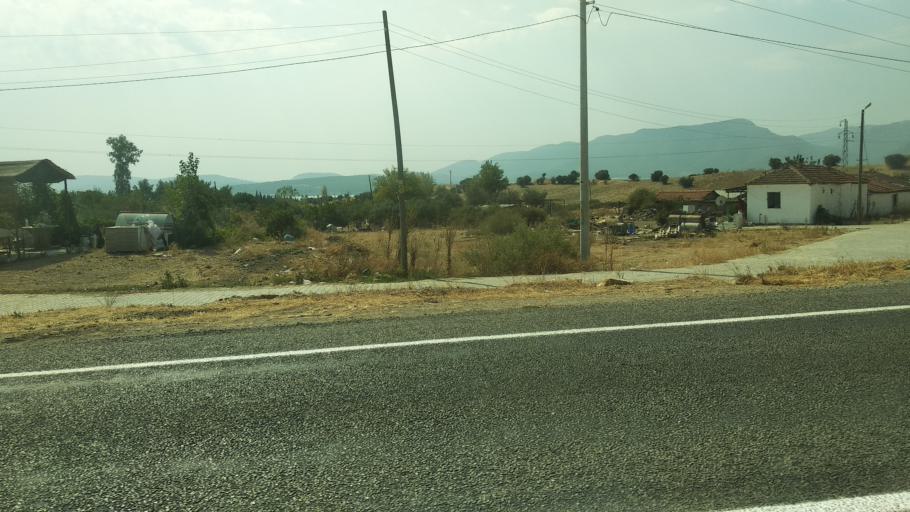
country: TR
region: Izmir
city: Degirmendere
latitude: 38.1797
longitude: 27.1137
